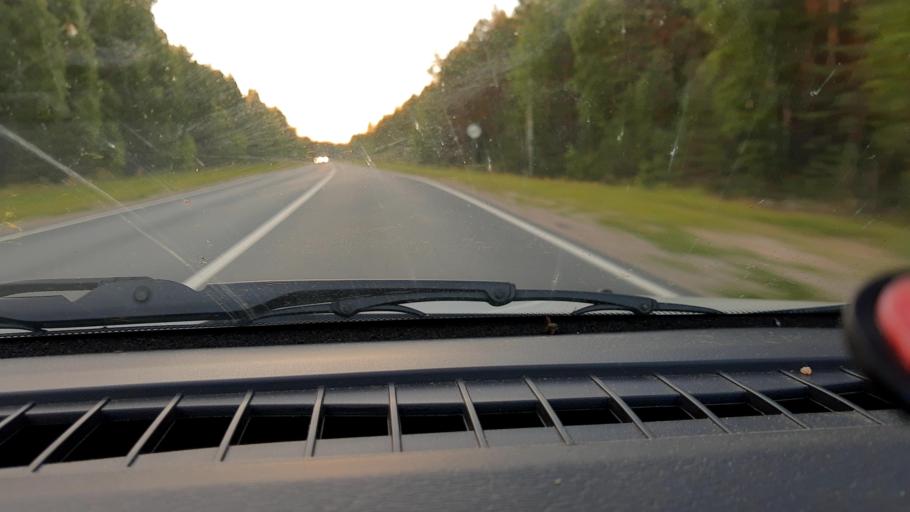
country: RU
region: Nizjnij Novgorod
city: Krasnyye Baki
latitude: 57.2050
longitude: 45.4608
